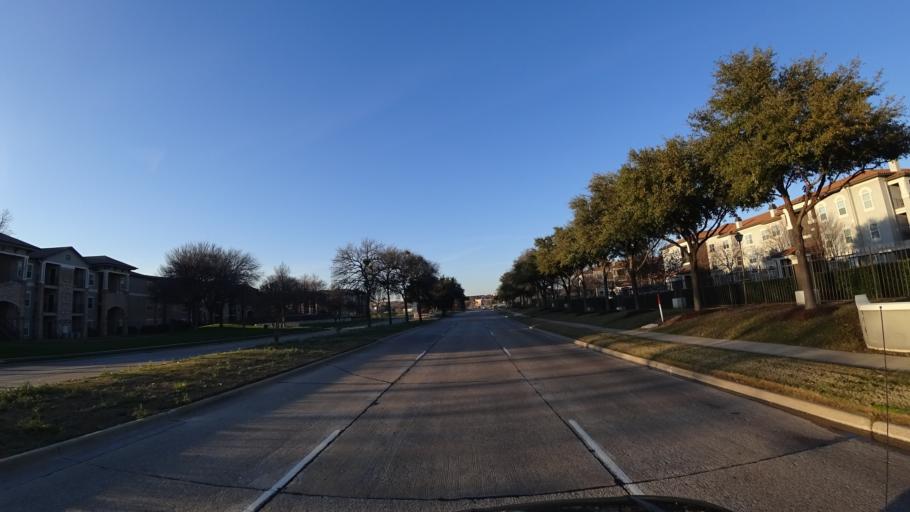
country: US
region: Texas
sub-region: Denton County
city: Lewisville
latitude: 32.9955
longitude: -96.9756
